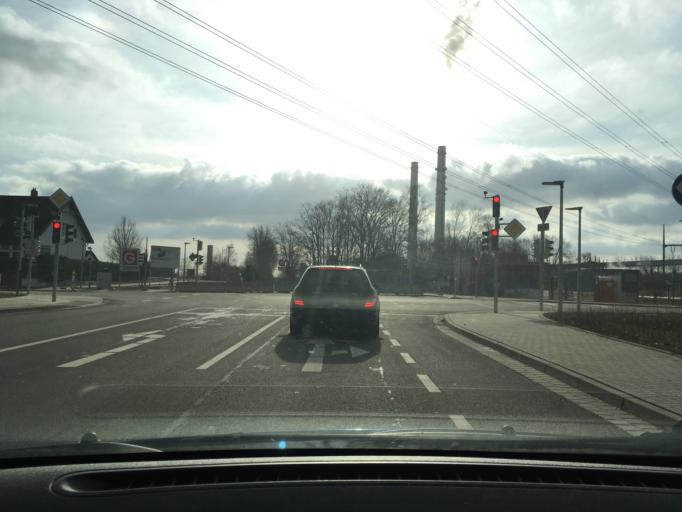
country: DE
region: Schleswig-Holstein
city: Wedel
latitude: 53.5718
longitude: 9.7305
